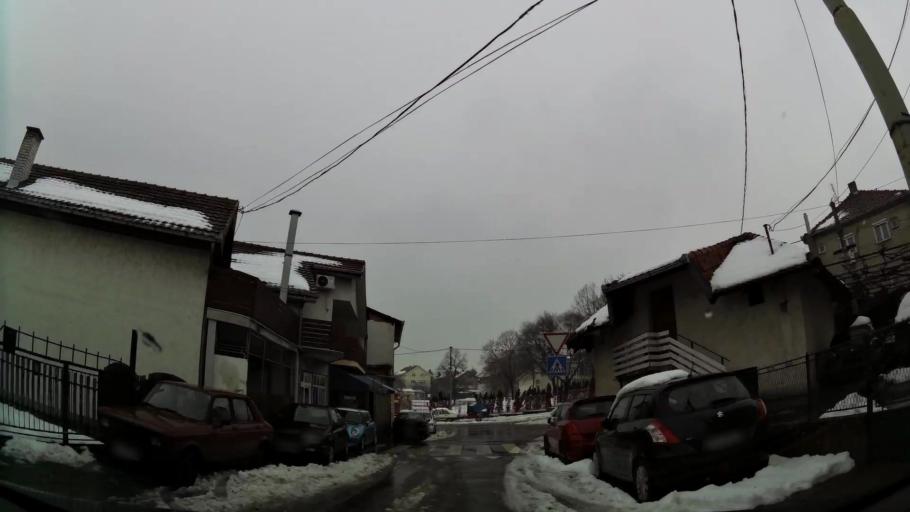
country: RS
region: Central Serbia
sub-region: Belgrade
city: Zemun
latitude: 44.8412
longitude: 20.3721
